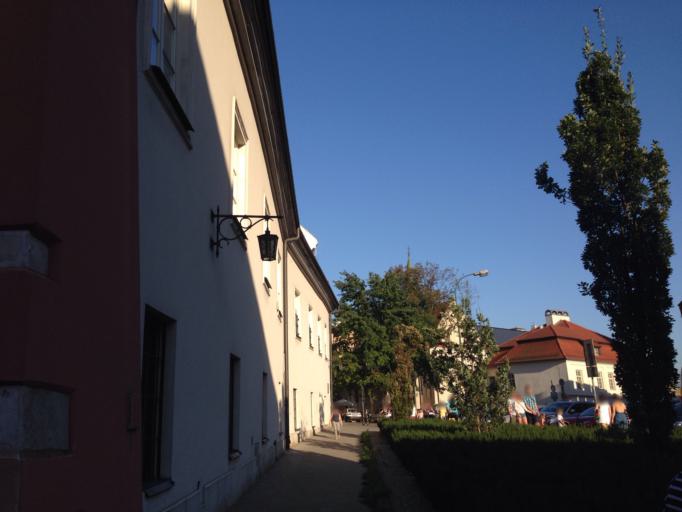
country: PL
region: Lesser Poland Voivodeship
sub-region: Krakow
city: Krakow
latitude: 50.0556
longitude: 19.9369
